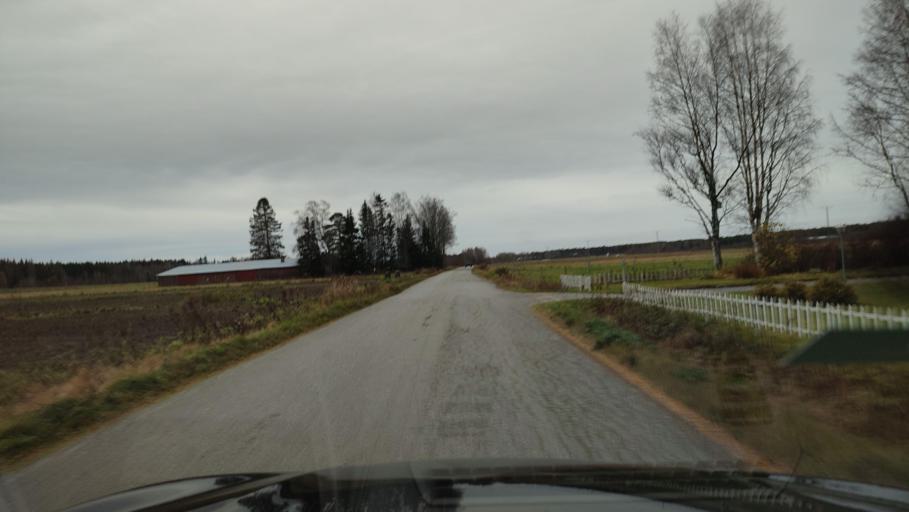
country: FI
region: Ostrobothnia
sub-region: Sydosterbotten
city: Naerpes
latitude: 62.4103
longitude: 21.3986
